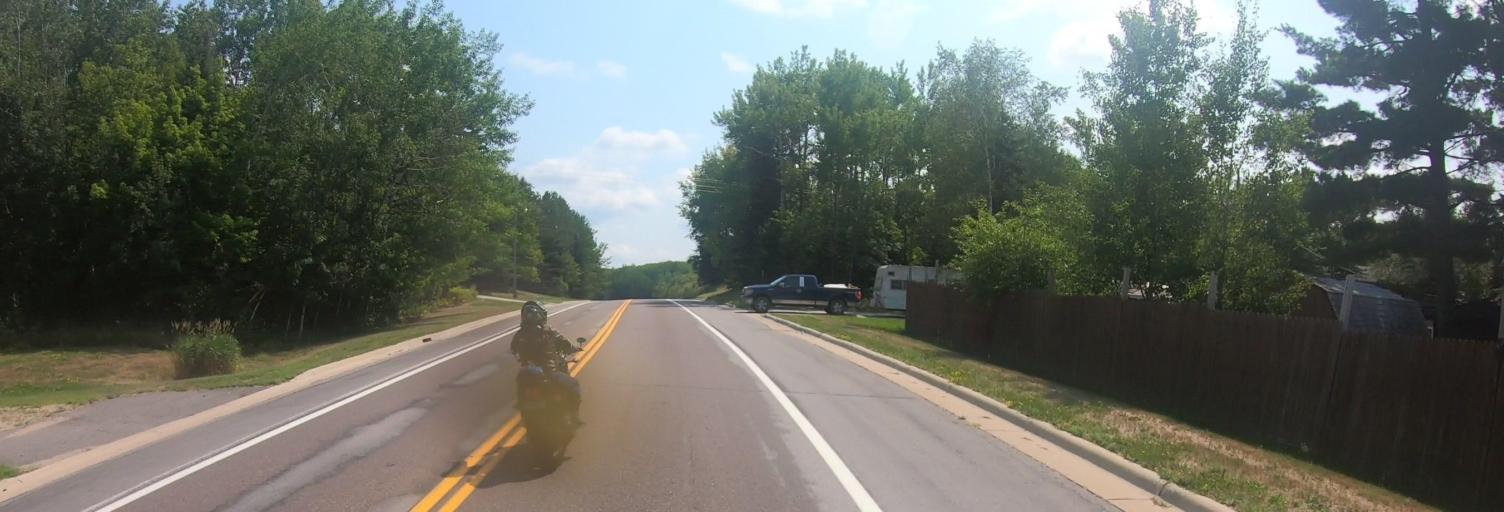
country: US
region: Minnesota
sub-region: Saint Louis County
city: Mountain Iron
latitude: 48.0503
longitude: -92.8280
